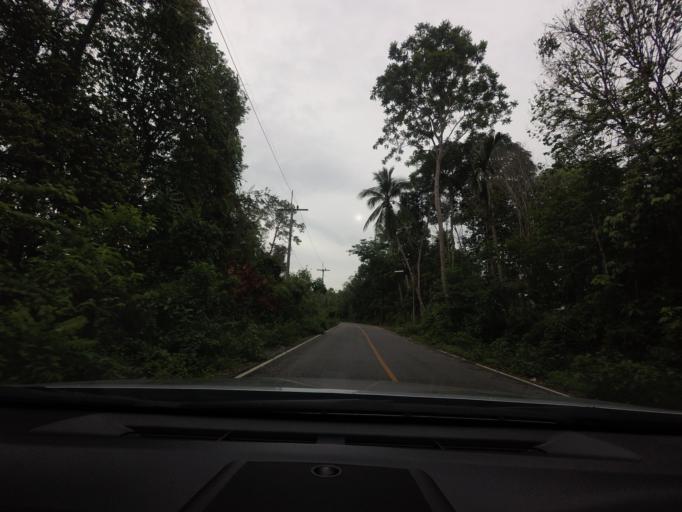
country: TH
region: Narathiwat
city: Rueso
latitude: 6.4137
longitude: 101.5188
